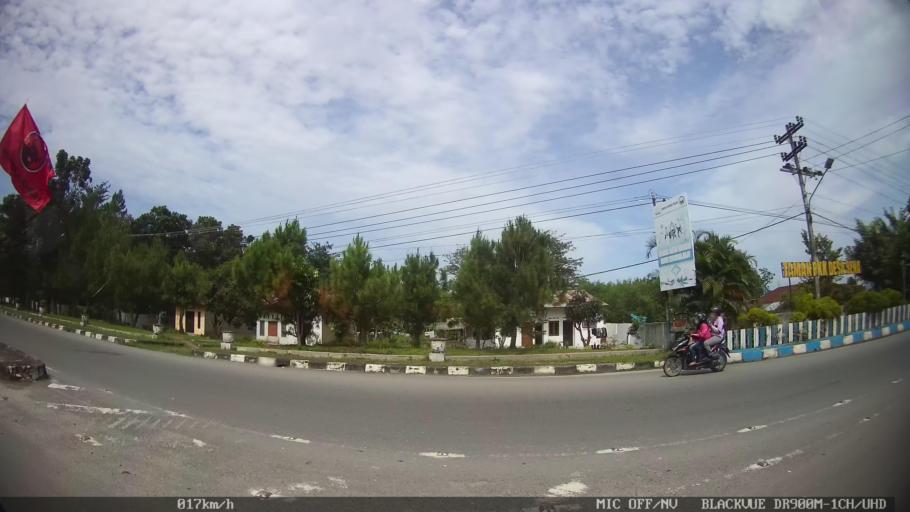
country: ID
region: North Sumatra
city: Percut
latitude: 3.5960
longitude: 98.8073
